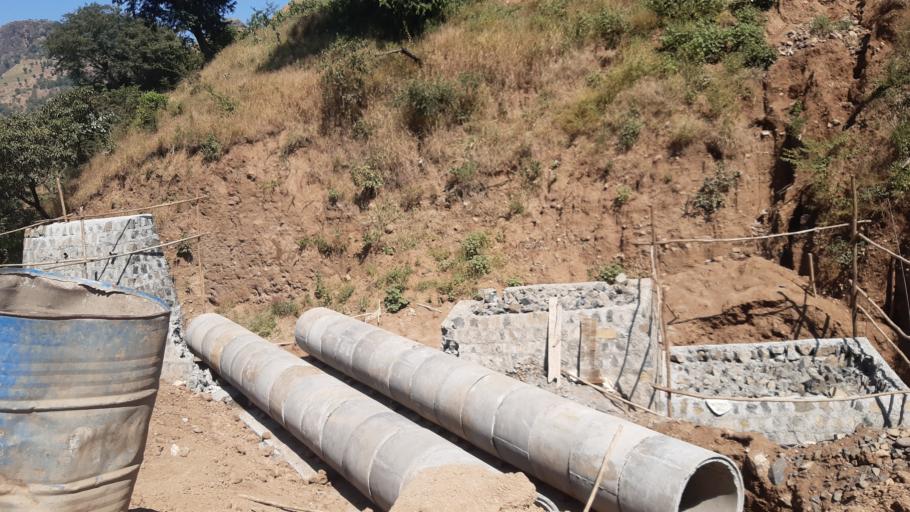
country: ET
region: Amhara
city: Dabat
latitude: 13.1924
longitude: 37.5724
